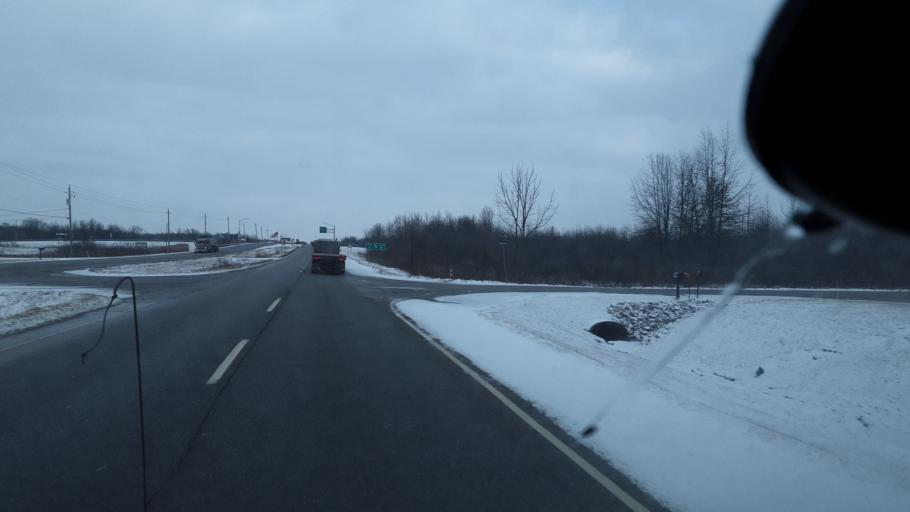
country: US
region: Ohio
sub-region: Trumbull County
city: Lordstown
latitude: 41.1114
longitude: -80.8875
